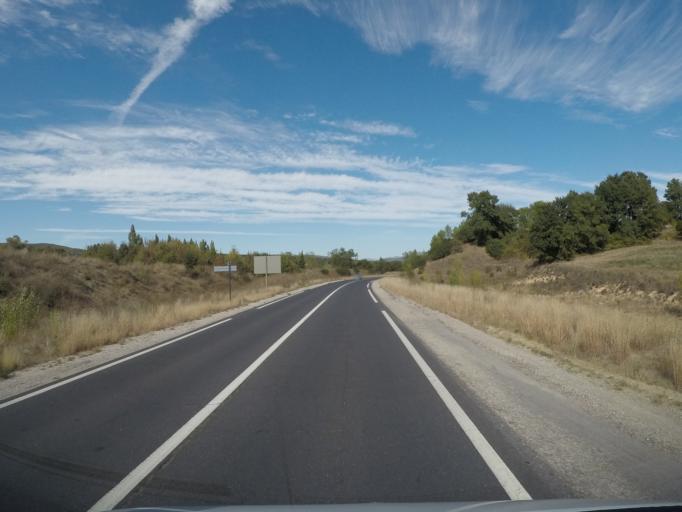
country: FR
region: Languedoc-Roussillon
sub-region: Departement de l'Herault
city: Saint-Martin-de-Londres
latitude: 43.7906
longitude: 3.7367
